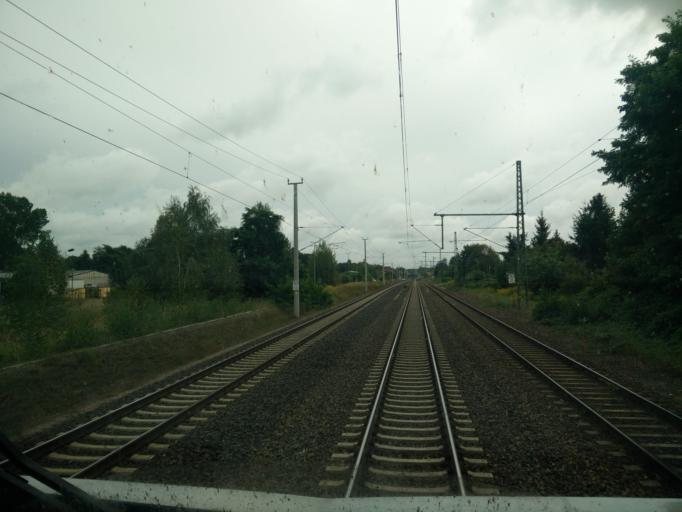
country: DE
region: Brandenburg
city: Halbe
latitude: 52.1124
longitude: 13.6975
